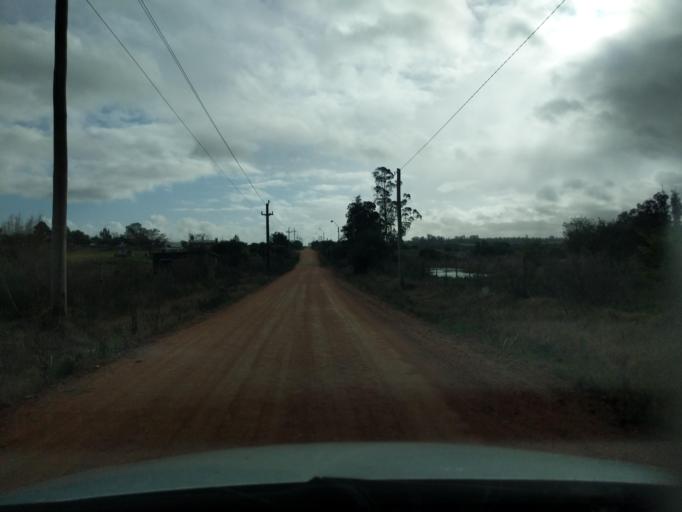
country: UY
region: Florida
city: Florida
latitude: -34.0678
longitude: -56.2196
